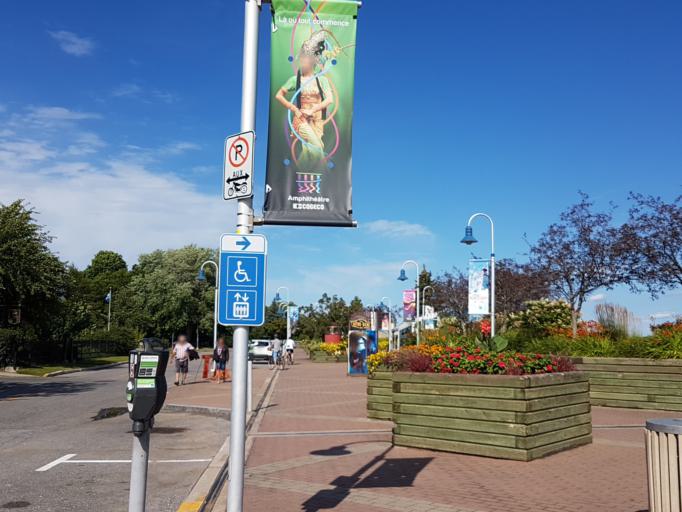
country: CA
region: Quebec
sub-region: Mauricie
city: Trois-Rivieres
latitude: 46.3421
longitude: -72.5376
